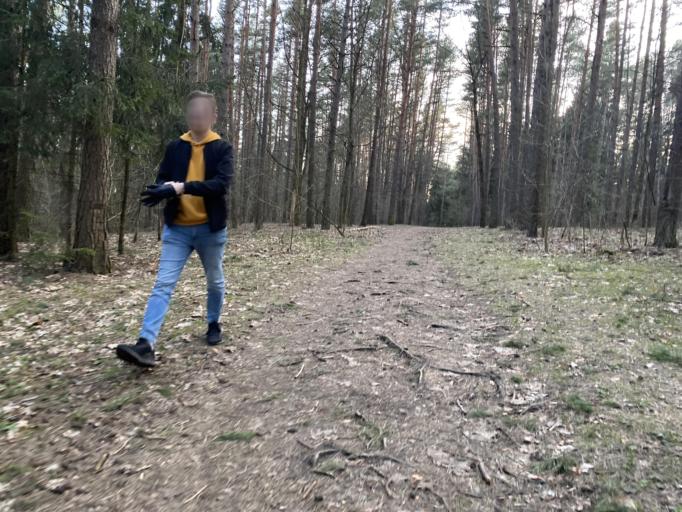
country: BY
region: Minsk
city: Borovlyany
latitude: 53.9476
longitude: 27.6522
